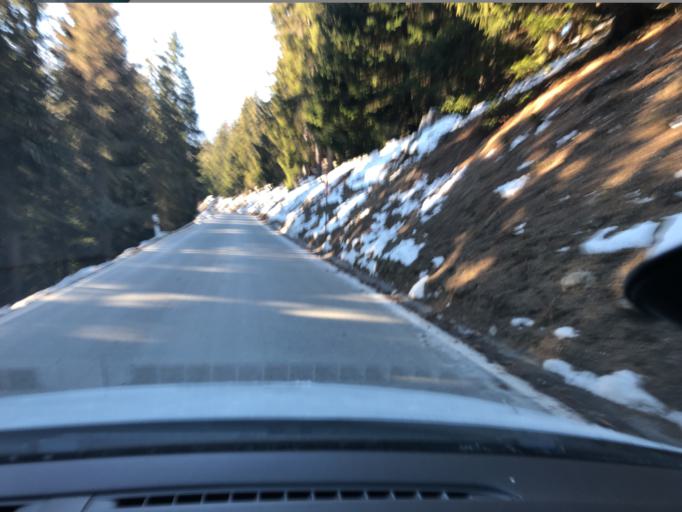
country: CH
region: Valais
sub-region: Goms District
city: Fiesch
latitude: 46.4124
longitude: 8.1484
